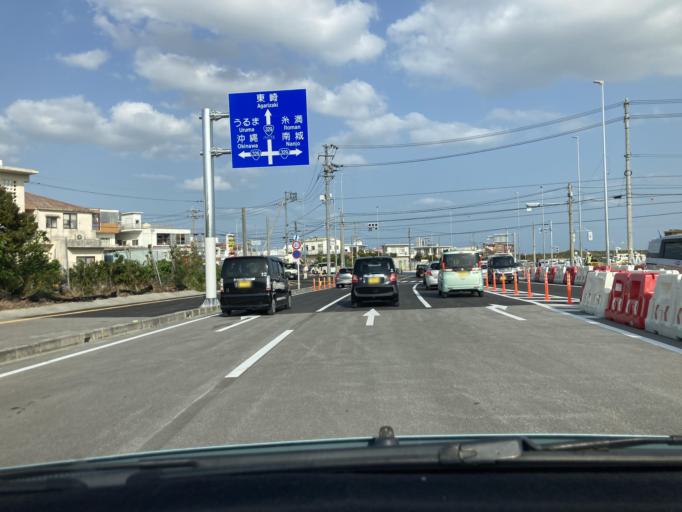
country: JP
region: Okinawa
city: Ginowan
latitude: 26.2121
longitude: 127.7595
